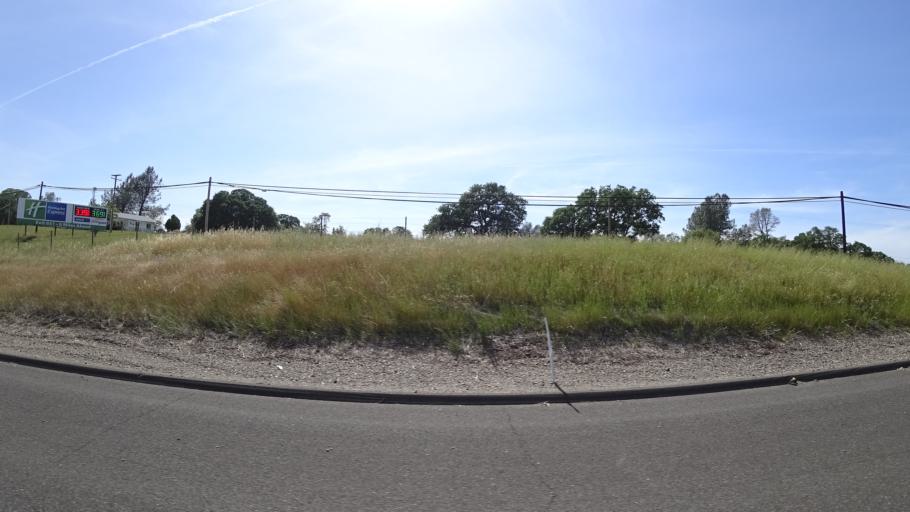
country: US
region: California
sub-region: Shasta County
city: Cottonwood
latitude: 40.2874
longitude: -122.2784
